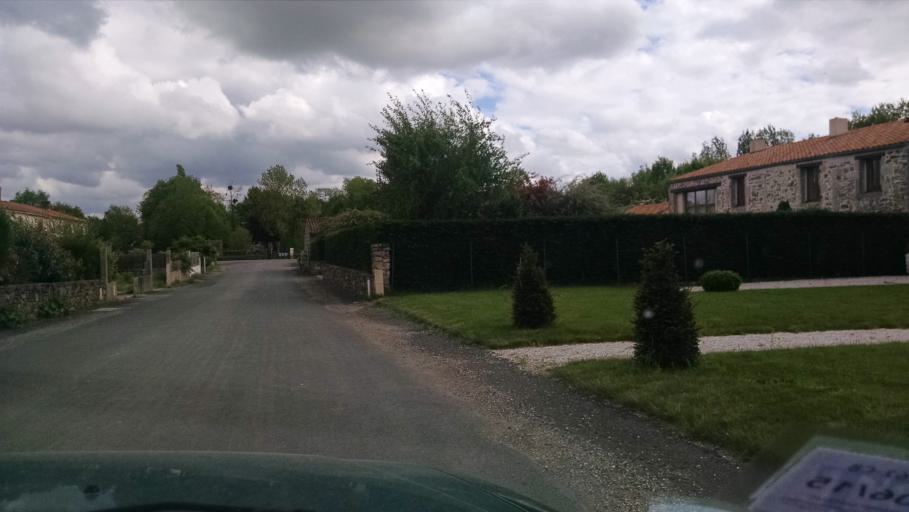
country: FR
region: Pays de la Loire
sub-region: Departement de la Vendee
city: Bouffere
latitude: 46.9728
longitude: -1.3439
